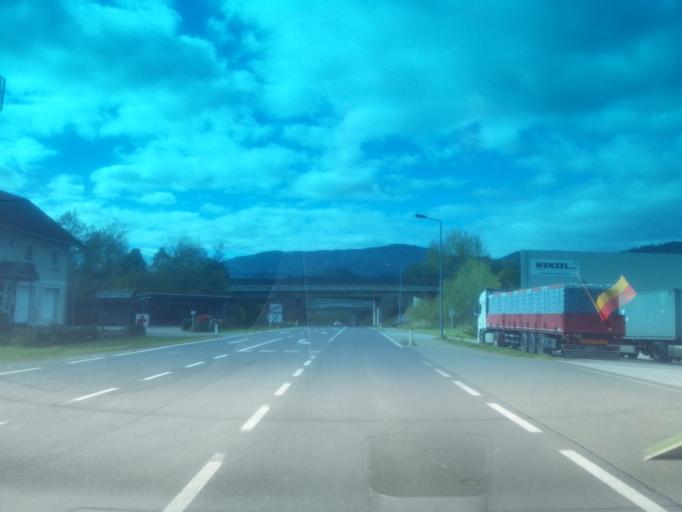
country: AT
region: Styria
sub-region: Politischer Bezirk Leoben
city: Sankt Michael in Obersteiermark
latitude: 47.3389
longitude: 15.0099
